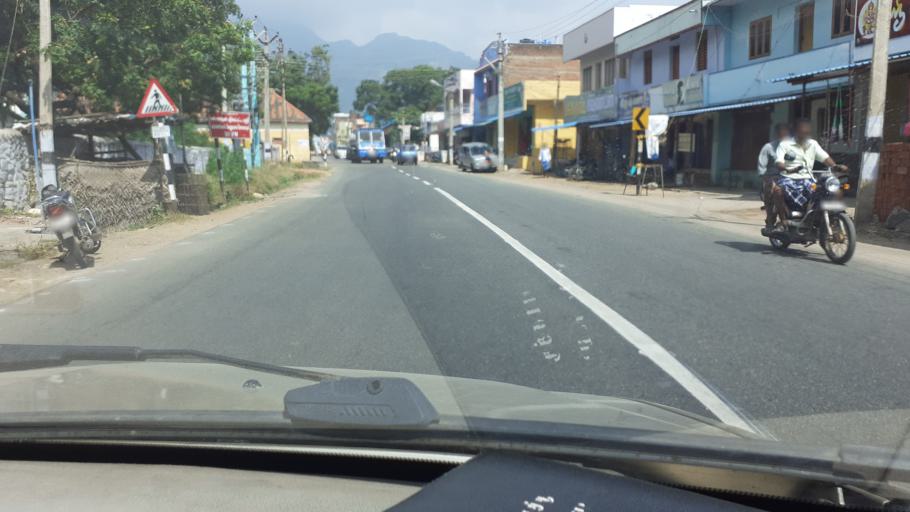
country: IN
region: Tamil Nadu
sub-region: Kanniyakumari
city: Suchindram
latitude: 8.2476
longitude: 77.5211
